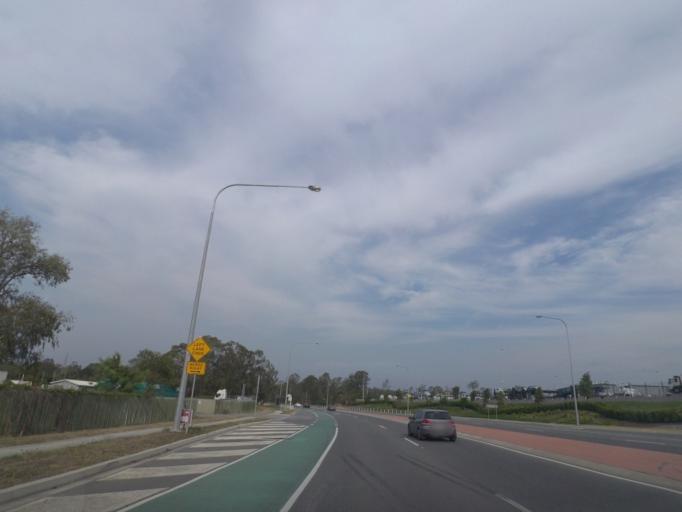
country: AU
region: Queensland
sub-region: Brisbane
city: Inala
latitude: -27.5981
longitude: 153.0123
